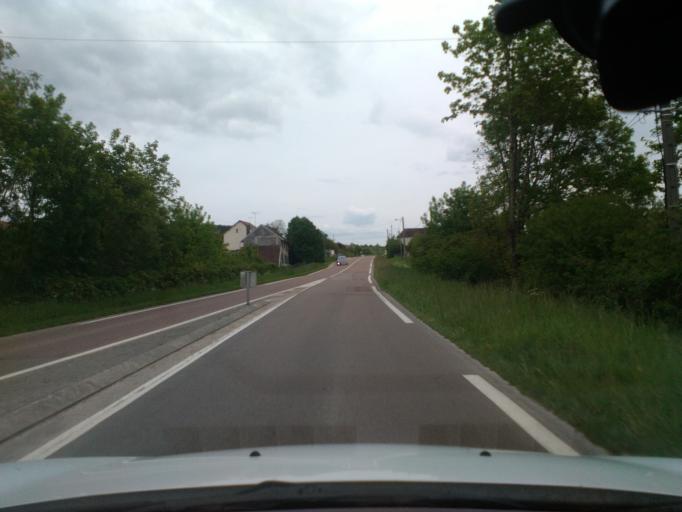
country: FR
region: Champagne-Ardenne
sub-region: Departement de l'Aube
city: Bar-sur-Aube
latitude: 48.2623
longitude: 4.6658
